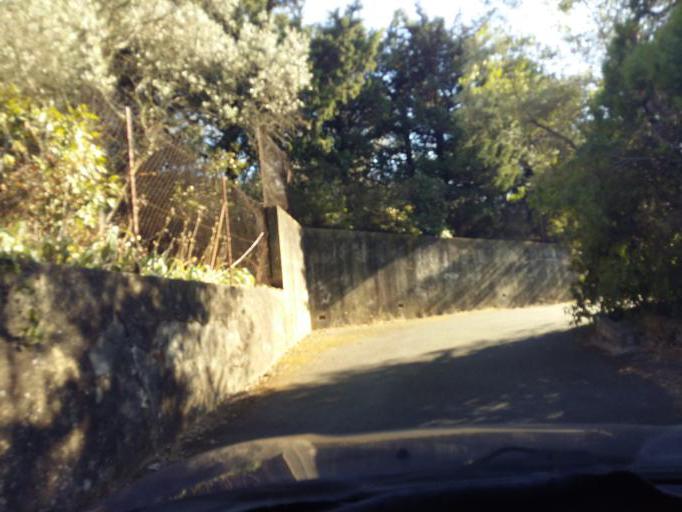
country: FR
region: Provence-Alpes-Cote d'Azur
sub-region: Departement du Vaucluse
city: Piolenc
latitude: 44.1758
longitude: 4.7629
